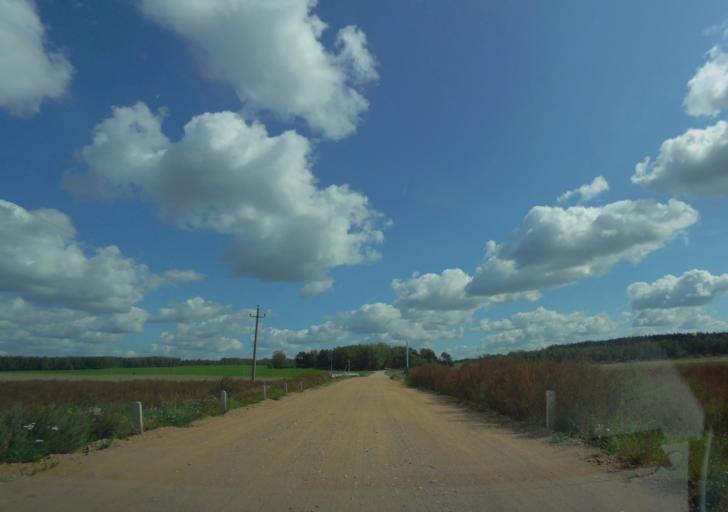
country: BY
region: Minsk
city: Horad Barysaw
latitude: 54.4265
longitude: 28.4494
